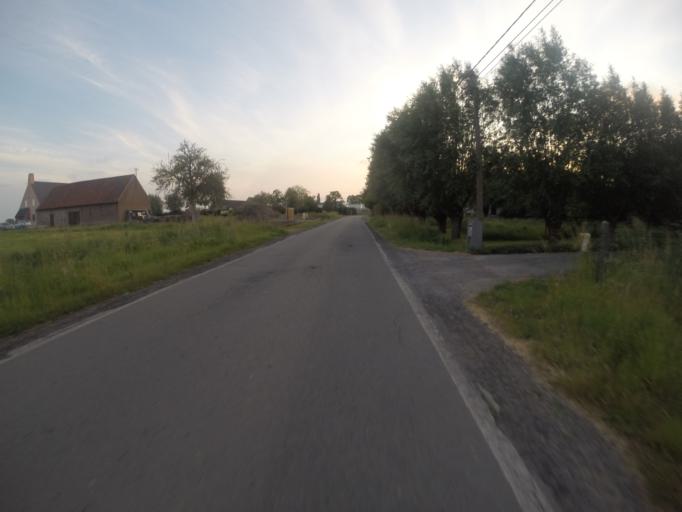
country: BE
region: Flanders
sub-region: Provincie Oost-Vlaanderen
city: Zomergem
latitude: 51.1119
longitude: 3.5287
